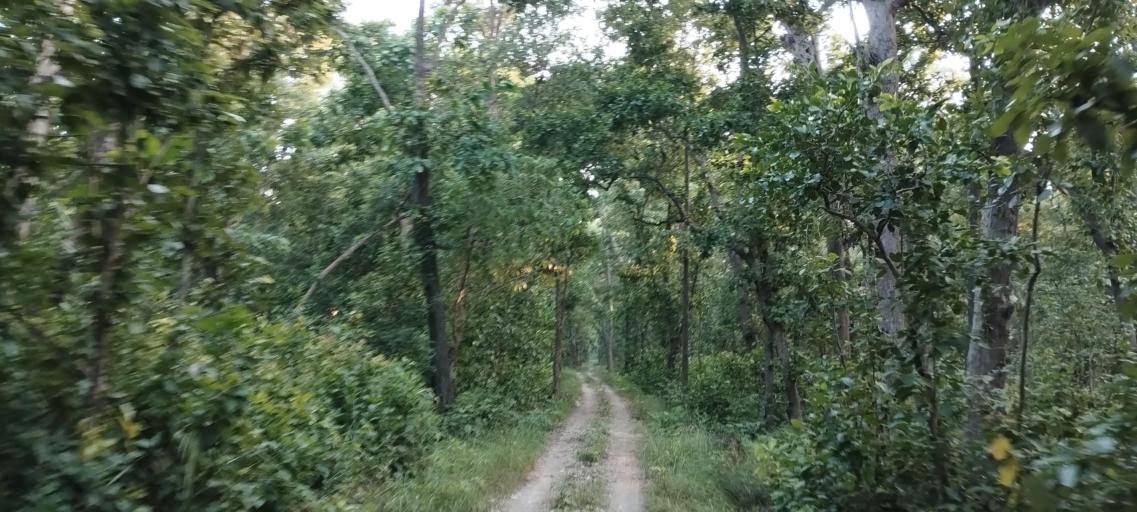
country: NP
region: Far Western
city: Tikapur
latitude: 28.4896
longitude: 81.2652
